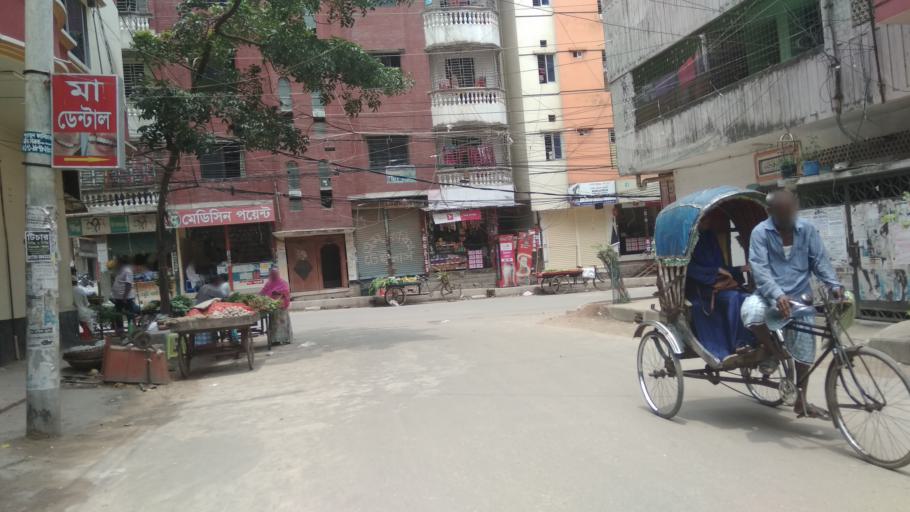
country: BD
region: Dhaka
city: Azimpur
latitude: 23.8126
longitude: 90.3697
